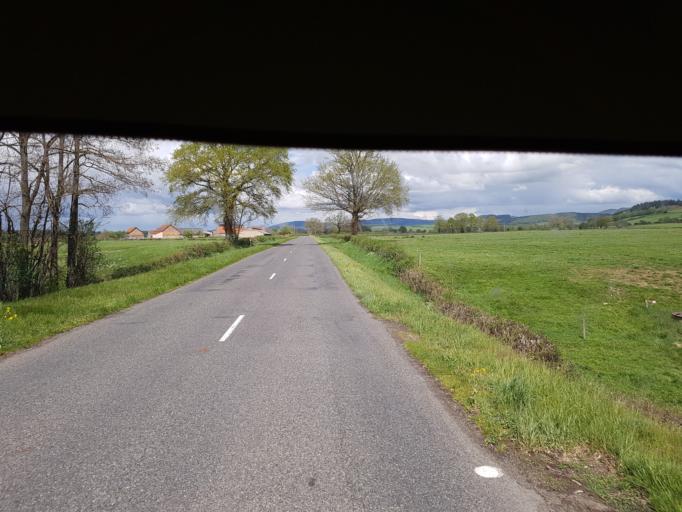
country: FR
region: Bourgogne
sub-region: Departement de Saone-et-Loire
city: Etang-sur-Arroux
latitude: 46.8147
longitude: 4.1627
